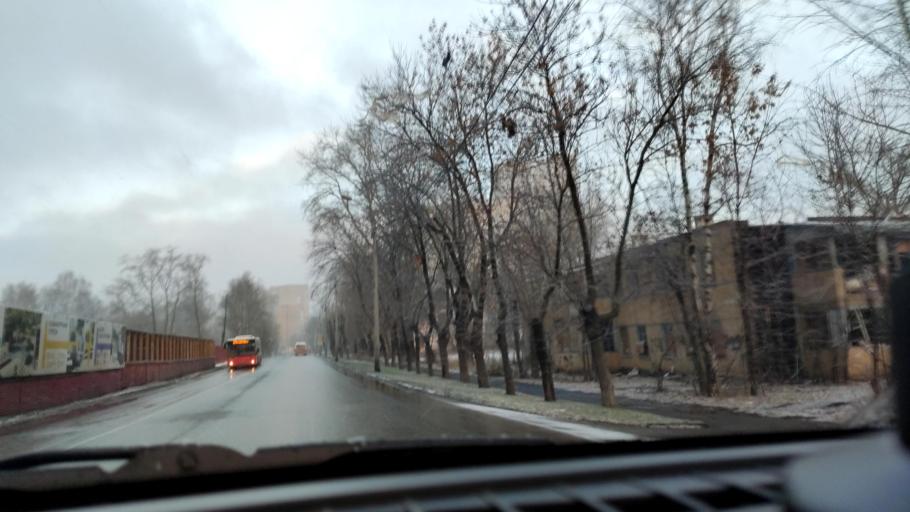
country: RU
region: Perm
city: Perm
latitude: 57.9990
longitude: 56.1854
